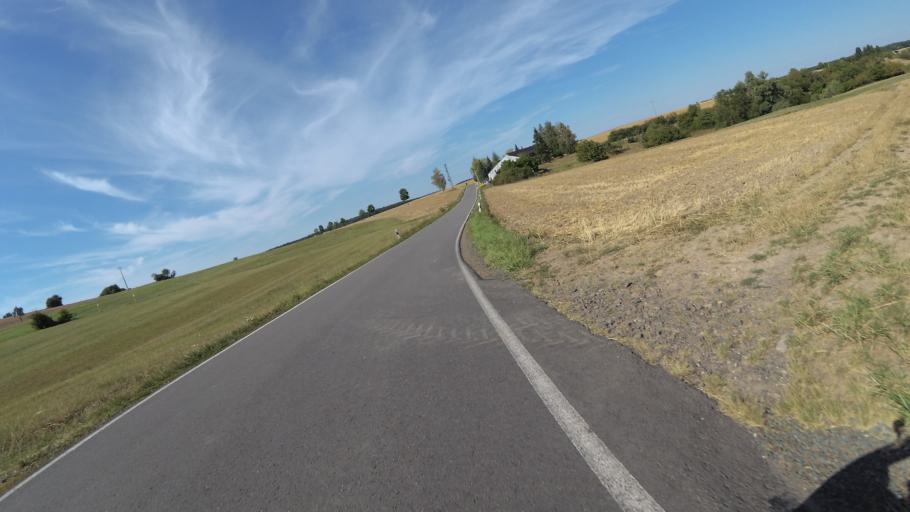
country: DE
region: Rheinland-Pfalz
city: Hornbach
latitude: 49.1729
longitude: 7.3014
